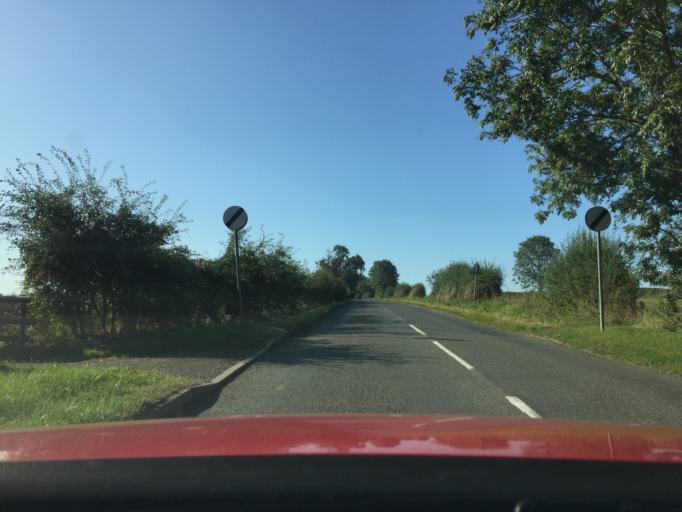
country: GB
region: England
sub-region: Leicestershire
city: Queniborough
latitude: 52.6668
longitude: -1.0211
